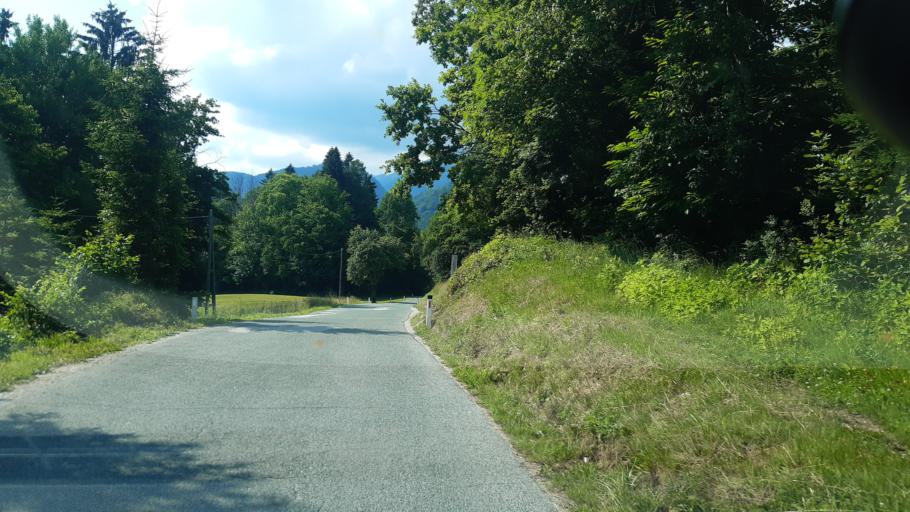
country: SI
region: Radovljica
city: Radovljica
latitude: 46.3719
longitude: 14.2187
